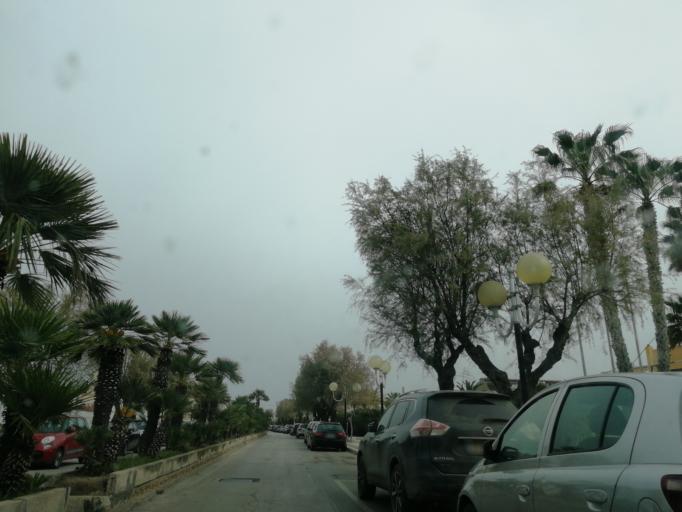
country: IT
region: Apulia
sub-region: Provincia di Barletta - Andria - Trani
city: Barletta
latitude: 41.3210
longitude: 16.2957
